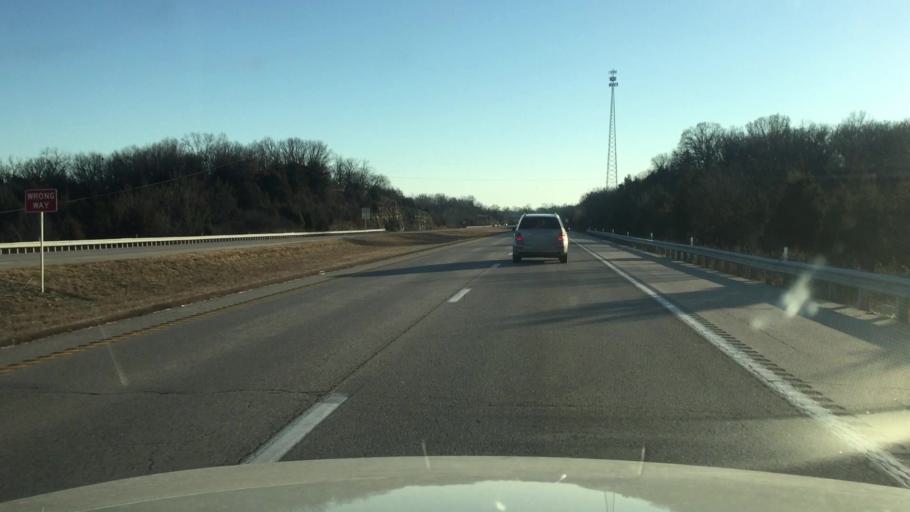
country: US
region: Missouri
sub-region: Cole County
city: Wardsville
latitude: 38.4837
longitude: -92.2721
